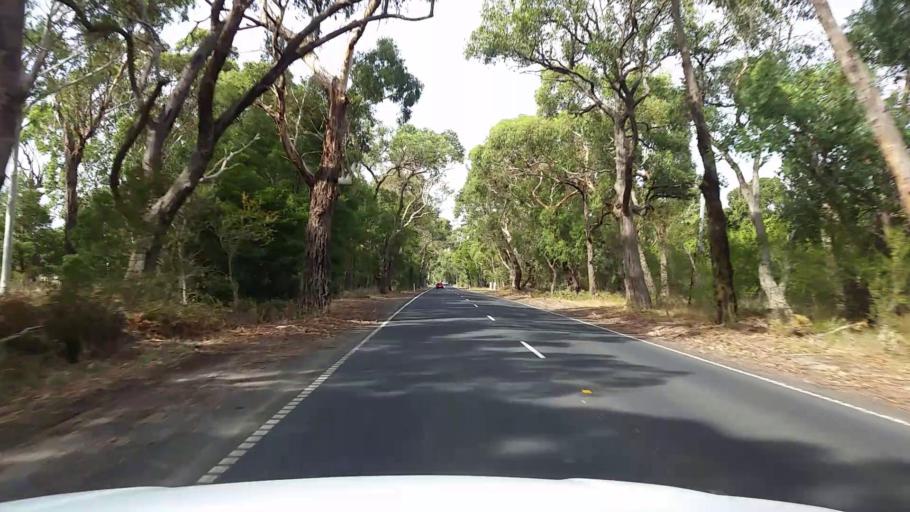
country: AU
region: Victoria
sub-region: Mornington Peninsula
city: Mount Martha
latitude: -38.2998
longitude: 145.0792
